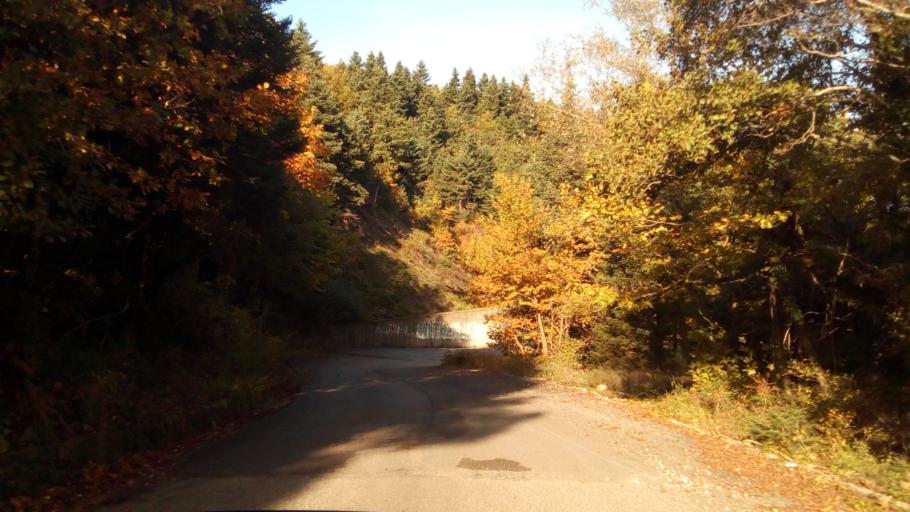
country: GR
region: West Greece
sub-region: Nomos Aitolias kai Akarnanias
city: Thermo
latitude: 38.6494
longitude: 21.8504
